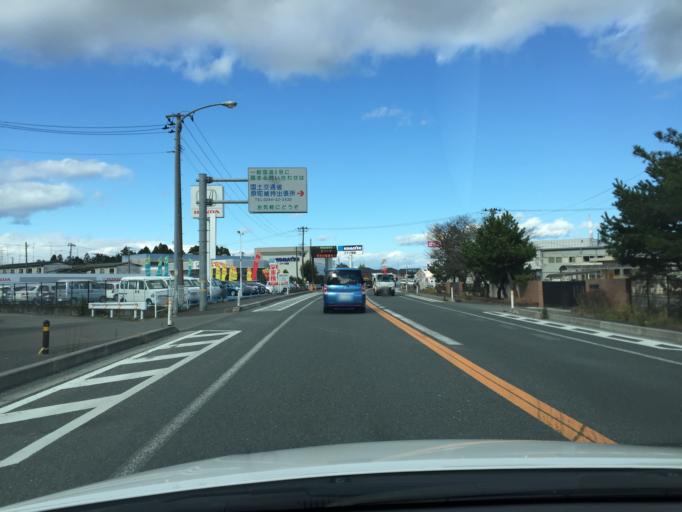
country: JP
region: Fukushima
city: Namie
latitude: 37.6327
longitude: 140.9858
